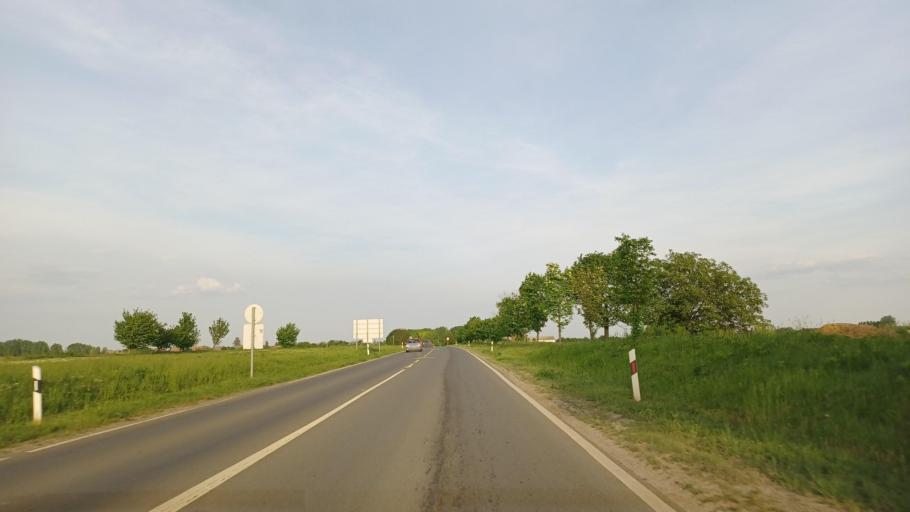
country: HU
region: Baranya
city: Boly
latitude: 45.9888
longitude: 18.5057
